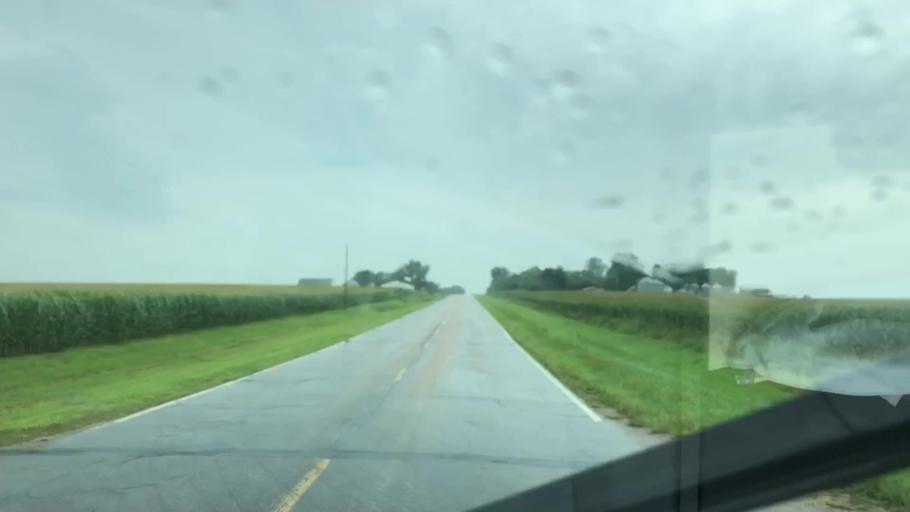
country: US
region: Iowa
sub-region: O'Brien County
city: Sanborn
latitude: 43.2725
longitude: -95.7038
